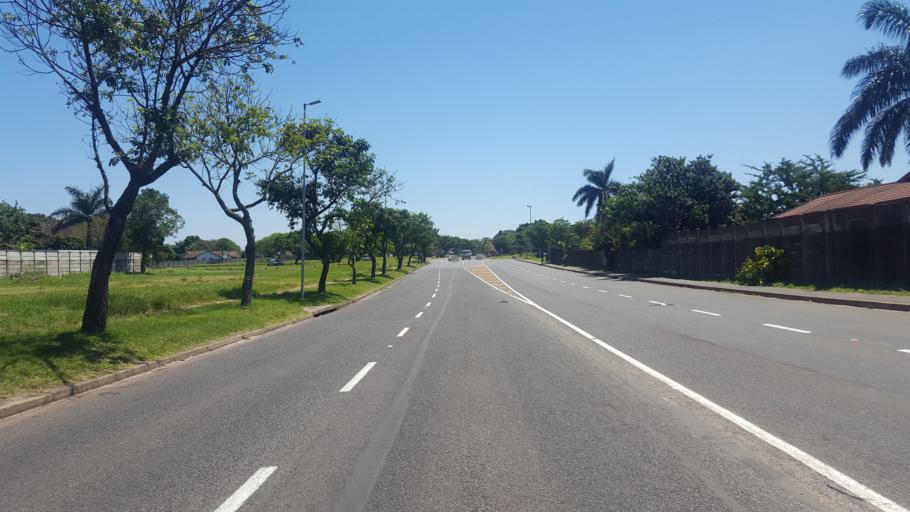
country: ZA
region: KwaZulu-Natal
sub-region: uThungulu District Municipality
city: Richards Bay
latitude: -28.7612
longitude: 32.0608
